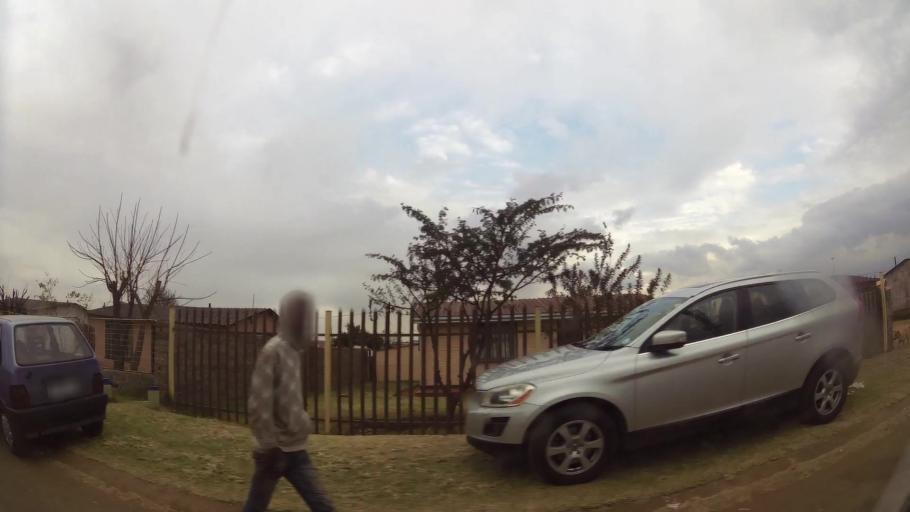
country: ZA
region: Gauteng
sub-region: Ekurhuleni Metropolitan Municipality
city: Germiston
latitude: -26.3802
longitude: 28.1358
